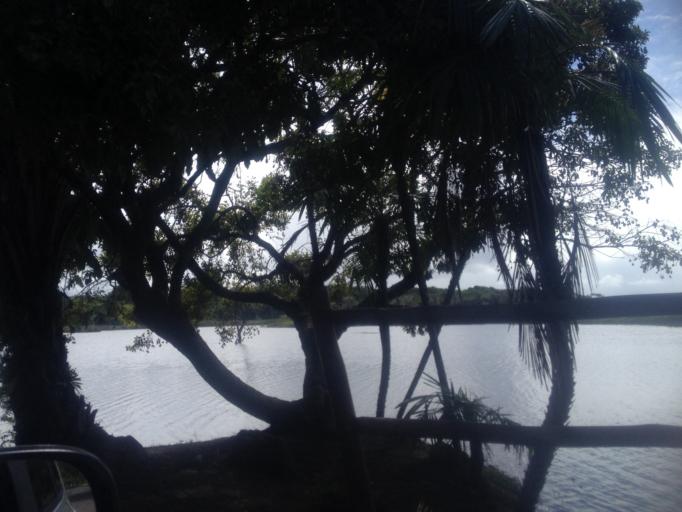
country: BR
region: Bahia
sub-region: Mata De Sao Joao
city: Mata de Sao Joao
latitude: -12.5774
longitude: -38.0142
